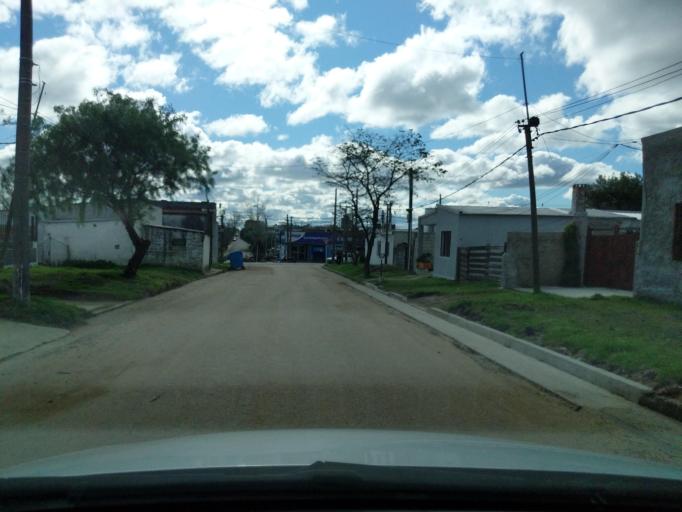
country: UY
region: Florida
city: Florida
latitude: -34.0939
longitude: -56.2297
